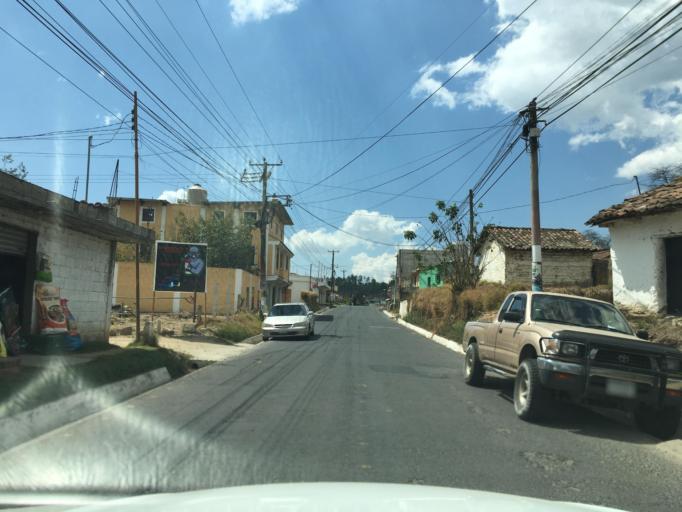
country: GT
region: Totonicapan
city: San Cristobal Totonicapan
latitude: 14.9082
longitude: -91.4528
